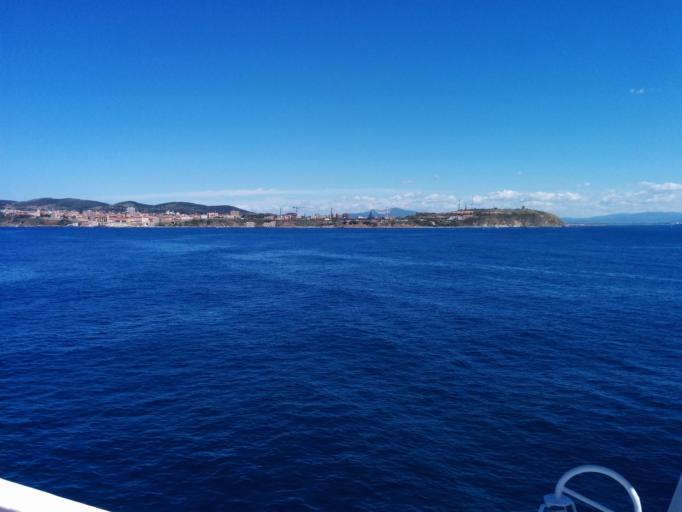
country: IT
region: Tuscany
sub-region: Provincia di Livorno
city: Piombino
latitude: 42.9038
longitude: 10.5274
